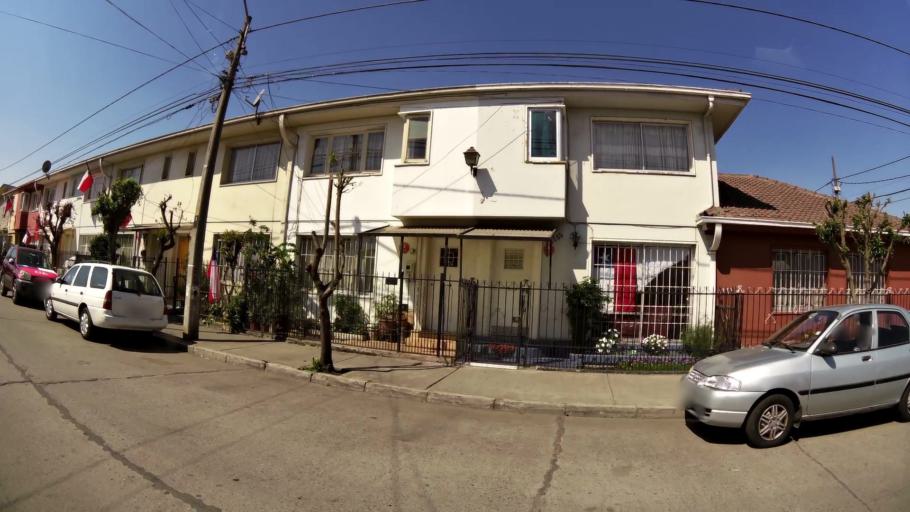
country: CL
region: Santiago Metropolitan
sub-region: Provincia de Santiago
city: Lo Prado
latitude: -33.4110
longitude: -70.6853
